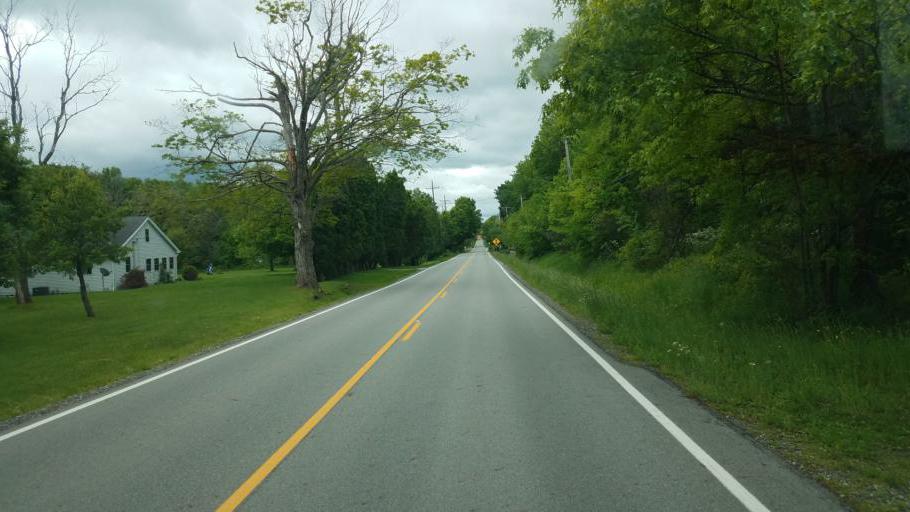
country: US
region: Ohio
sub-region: Portage County
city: Hiram
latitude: 41.3903
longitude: -81.1716
